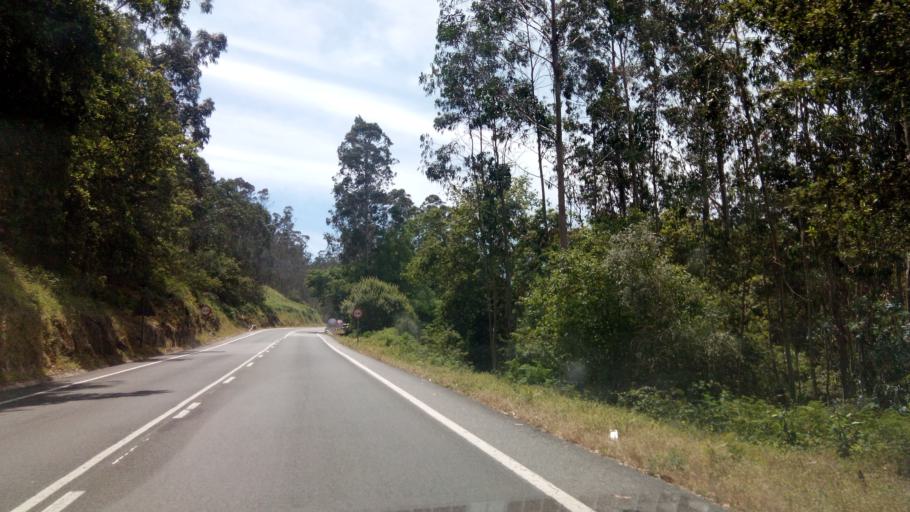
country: ES
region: Galicia
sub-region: Provincia de Pontevedra
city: Marin
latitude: 42.3371
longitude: -8.7130
